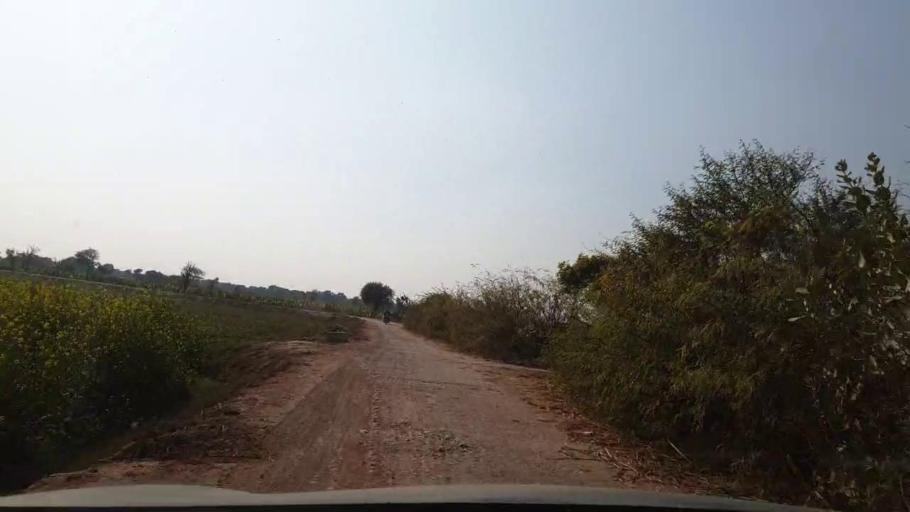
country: PK
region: Sindh
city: Tando Allahyar
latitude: 25.5515
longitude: 68.7767
